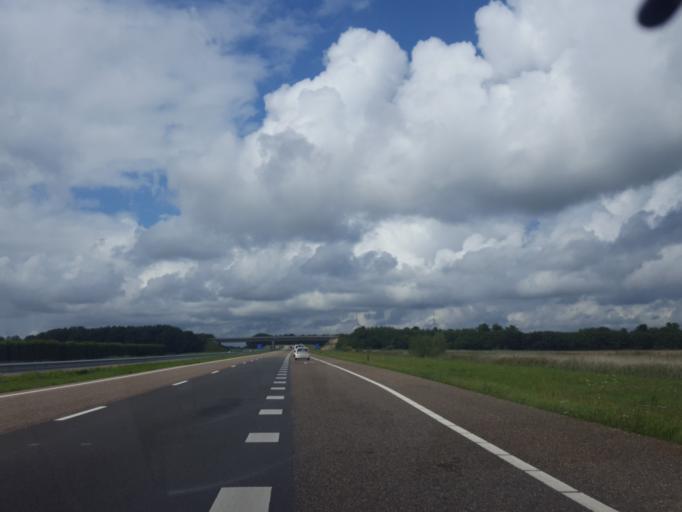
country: NL
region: North Brabant
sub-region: Gemeente Moerdijk
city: Willemstad
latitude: 51.6554
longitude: 4.4306
